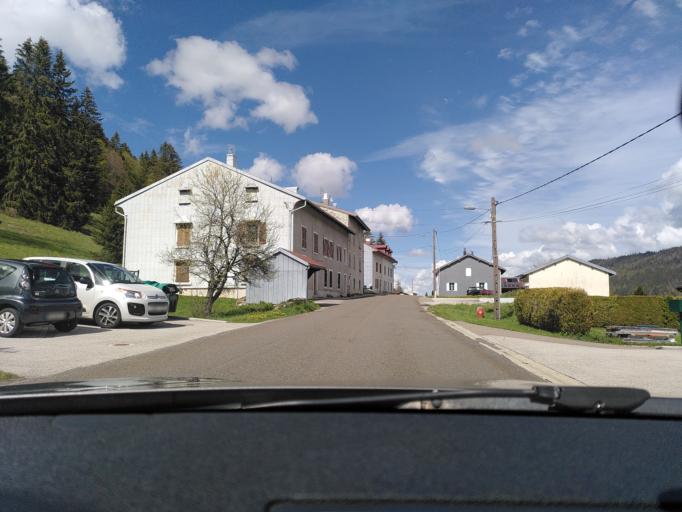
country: FR
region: Franche-Comte
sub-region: Departement du Jura
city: Les Rousses
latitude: 46.5253
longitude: 6.1145
